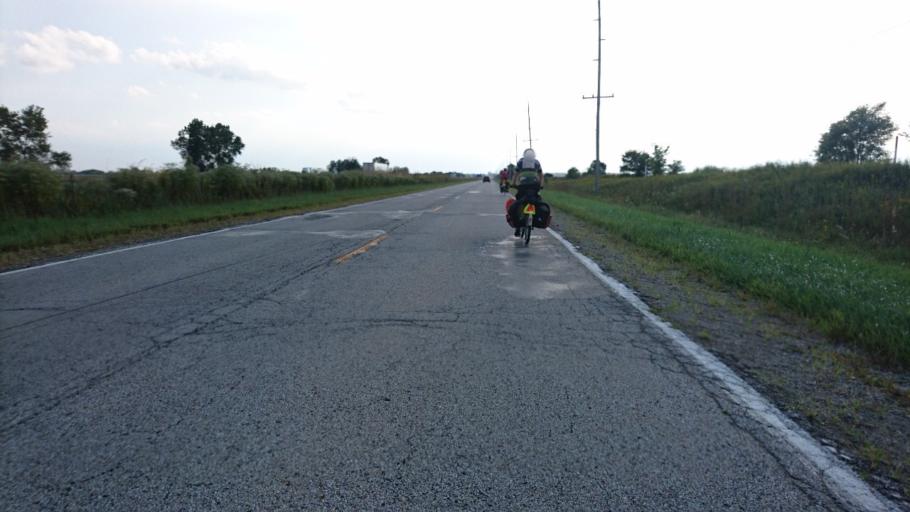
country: US
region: Illinois
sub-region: Logan County
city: Atlanta
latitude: 40.2938
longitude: -89.1936
